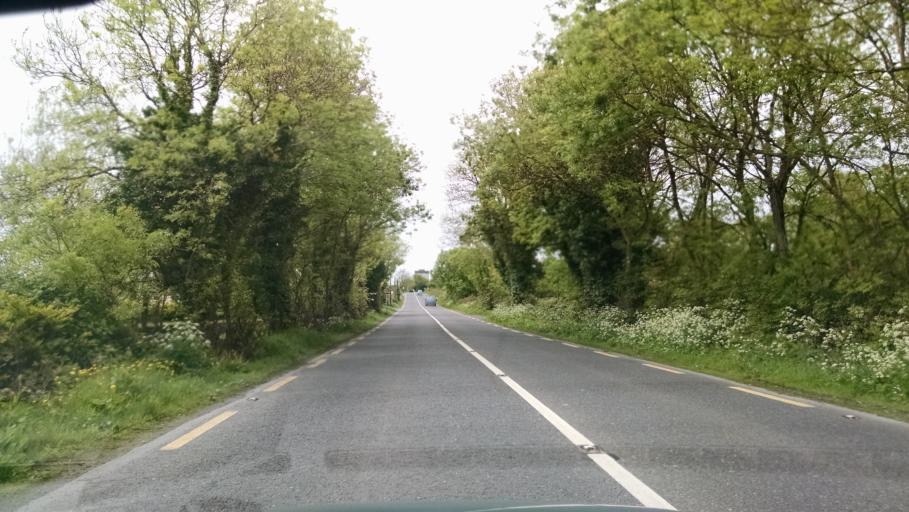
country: IE
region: Connaught
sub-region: County Galway
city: Gaillimh
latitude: 53.3129
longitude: -9.0238
